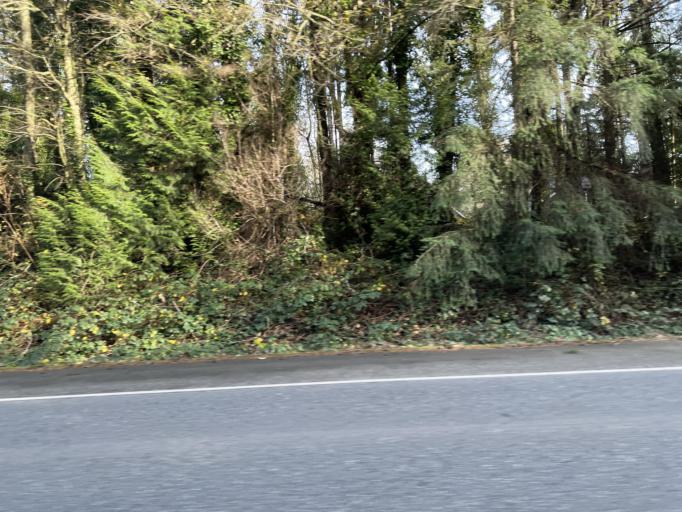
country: US
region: Washington
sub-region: Kitsap County
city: Bainbridge Island
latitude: 47.6402
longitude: -122.5134
